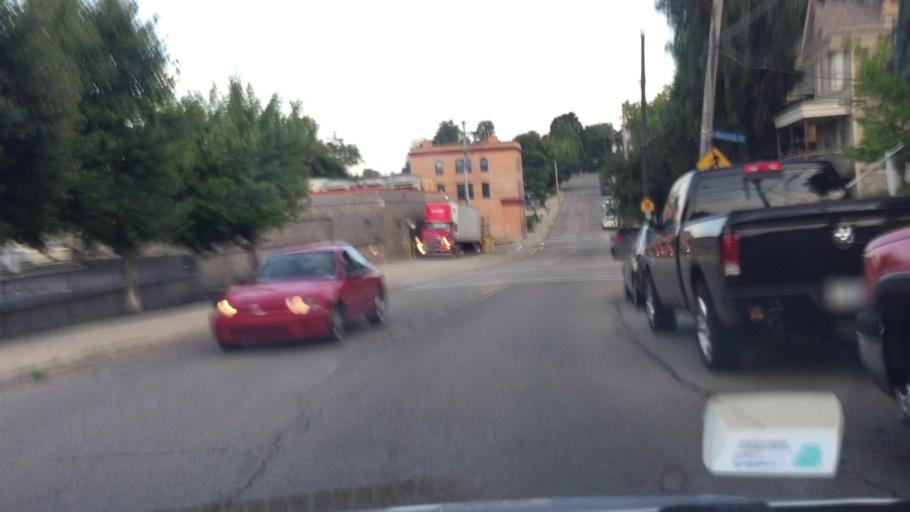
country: US
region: Pennsylvania
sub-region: Allegheny County
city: Homestead
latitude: 40.4227
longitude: -79.9300
